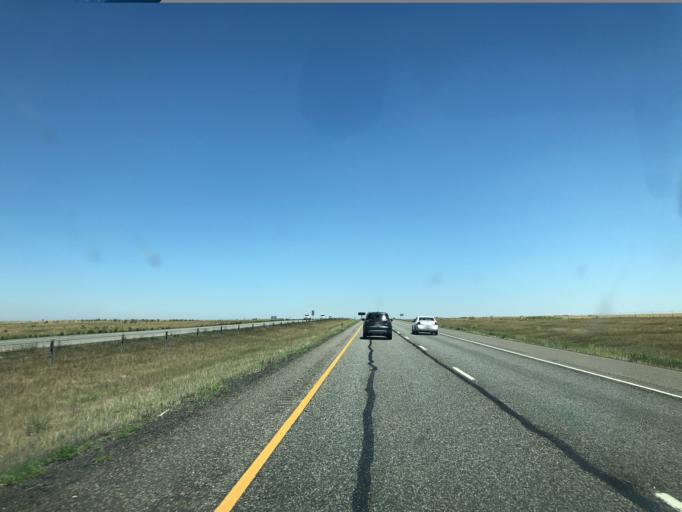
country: US
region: Colorado
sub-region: Adams County
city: Aurora
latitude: 39.7857
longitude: -104.7162
